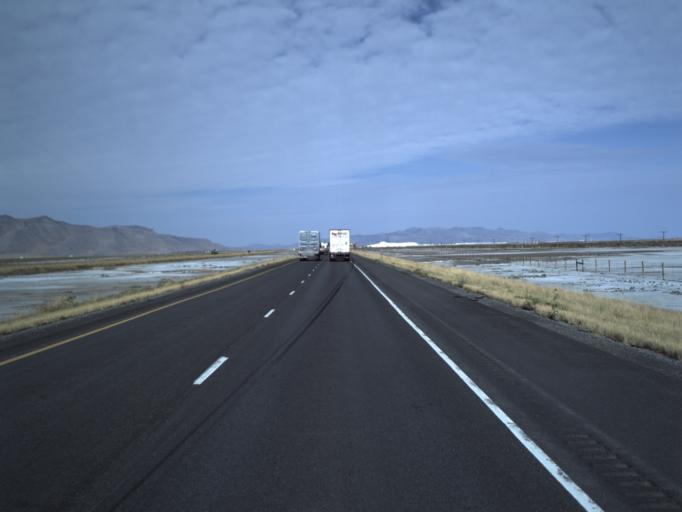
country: US
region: Utah
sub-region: Tooele County
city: Grantsville
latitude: 40.6964
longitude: -112.4758
